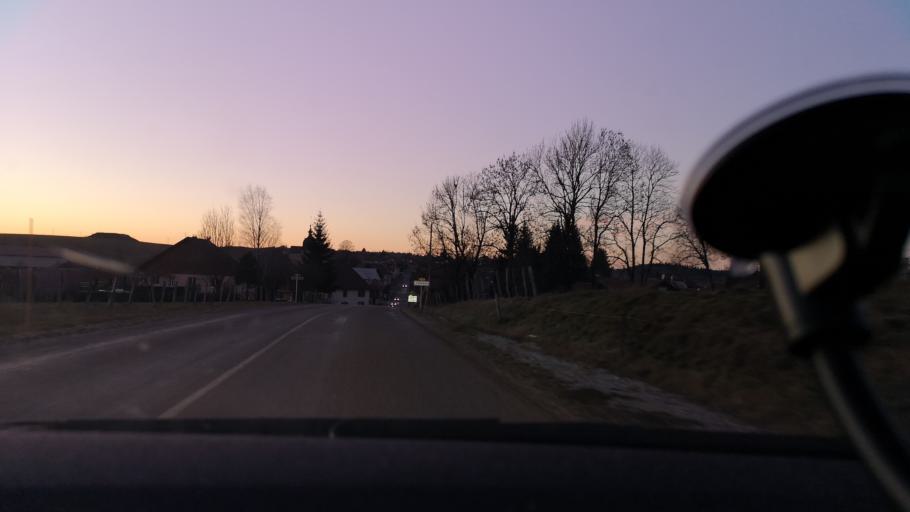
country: FR
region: Franche-Comte
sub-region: Departement du Doubs
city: Frasne
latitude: 46.8130
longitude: 6.0713
